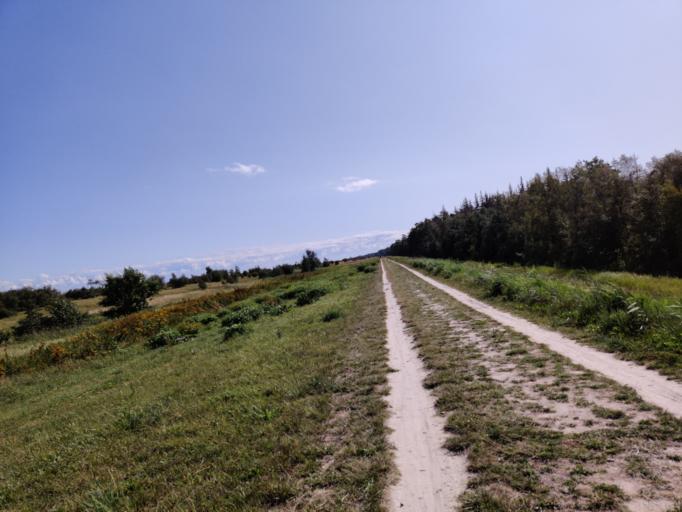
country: DK
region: Zealand
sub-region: Guldborgsund Kommune
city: Nykobing Falster
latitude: 54.6369
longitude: 11.9611
